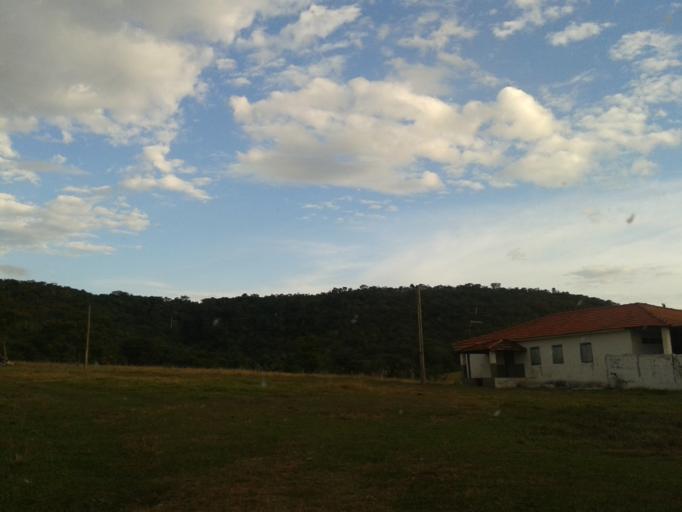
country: BR
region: Minas Gerais
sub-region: Campina Verde
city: Campina Verde
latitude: -19.3562
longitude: -49.6665
